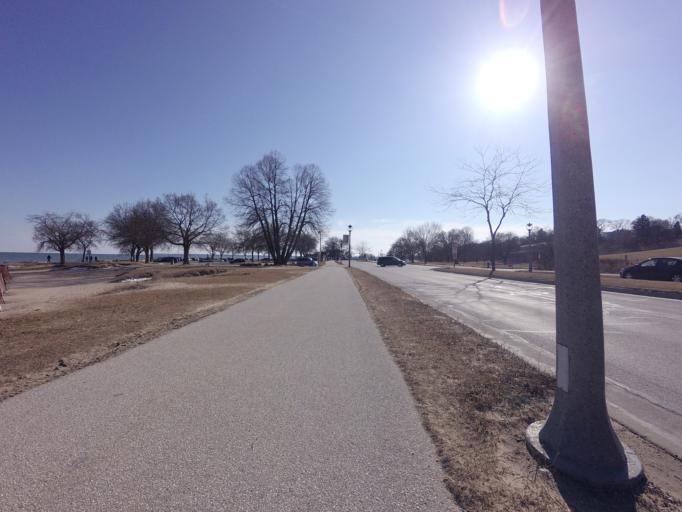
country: US
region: Wisconsin
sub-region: Milwaukee County
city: Shorewood
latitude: 43.0596
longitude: -87.8760
